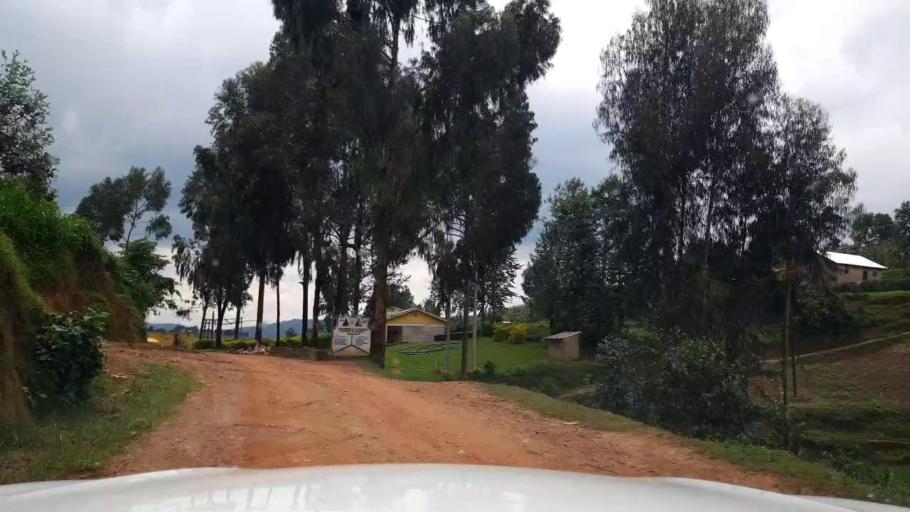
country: UG
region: Western Region
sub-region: Kabale District
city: Kabale
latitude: -1.4315
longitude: 29.8657
